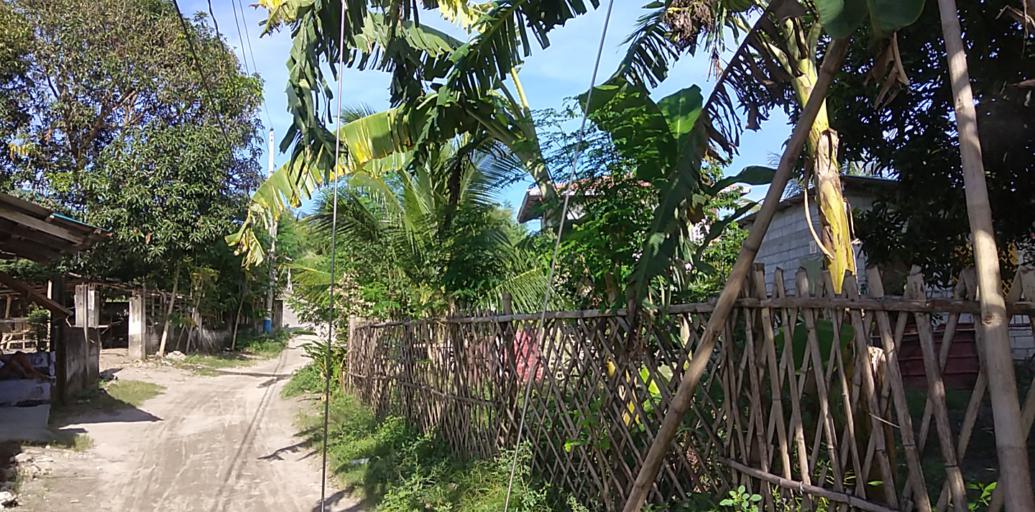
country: PH
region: Central Luzon
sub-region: Province of Pampanga
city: Porac
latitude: 15.0777
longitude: 120.5393
